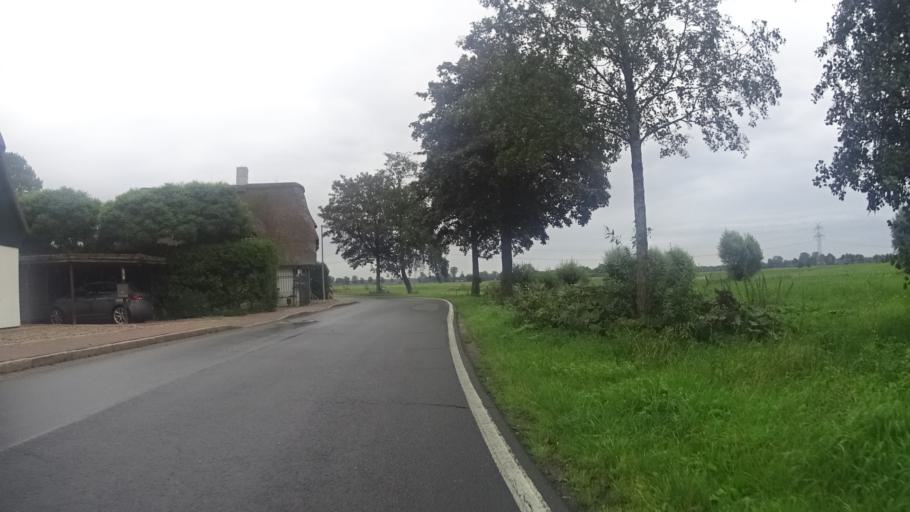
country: DE
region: Schleswig-Holstein
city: Altenmoor
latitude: 53.7893
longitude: 9.5776
